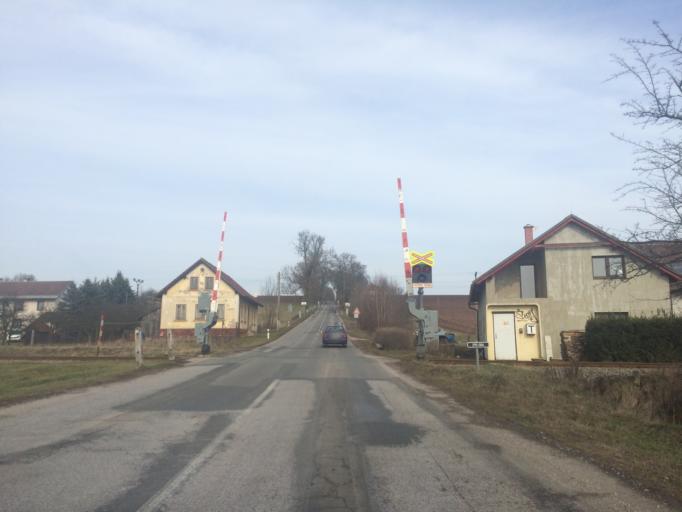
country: CZ
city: Horni Branna
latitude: 50.5936
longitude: 15.5943
